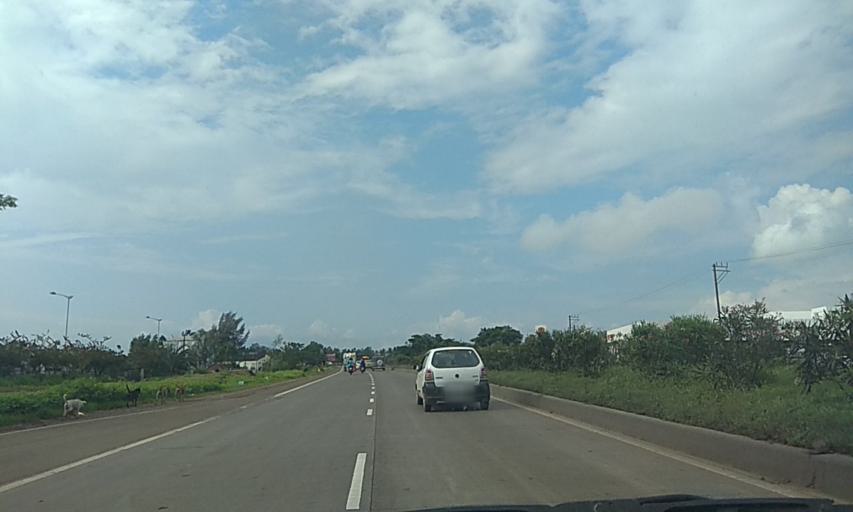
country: IN
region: Maharashtra
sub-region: Kolhapur
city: Kodoli
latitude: 16.8033
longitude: 74.2850
